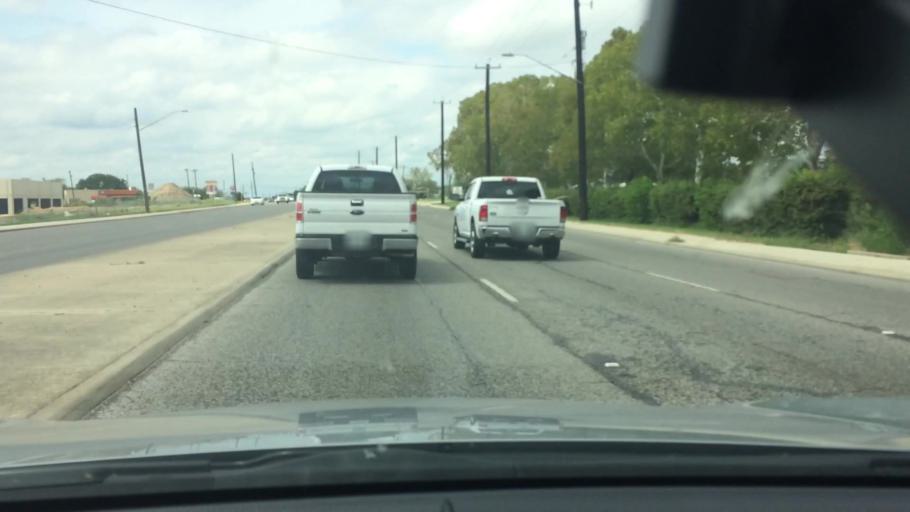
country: US
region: Texas
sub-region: Bexar County
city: San Antonio
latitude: 29.3524
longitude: -98.4554
